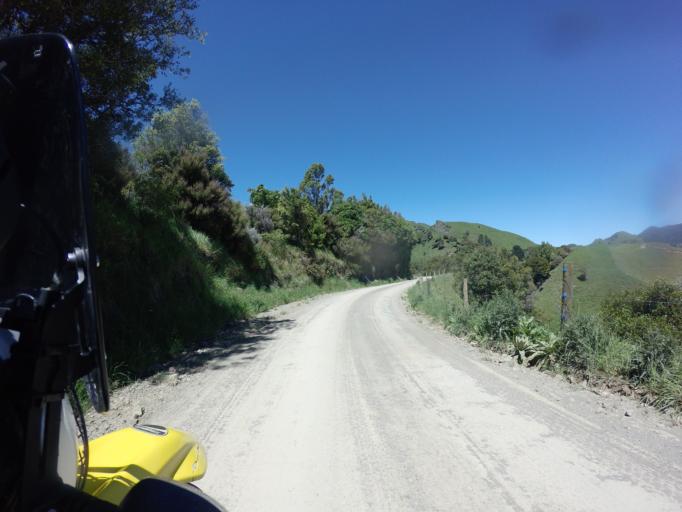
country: NZ
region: Bay of Plenty
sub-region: Opotiki District
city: Opotiki
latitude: -38.4025
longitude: 177.4560
